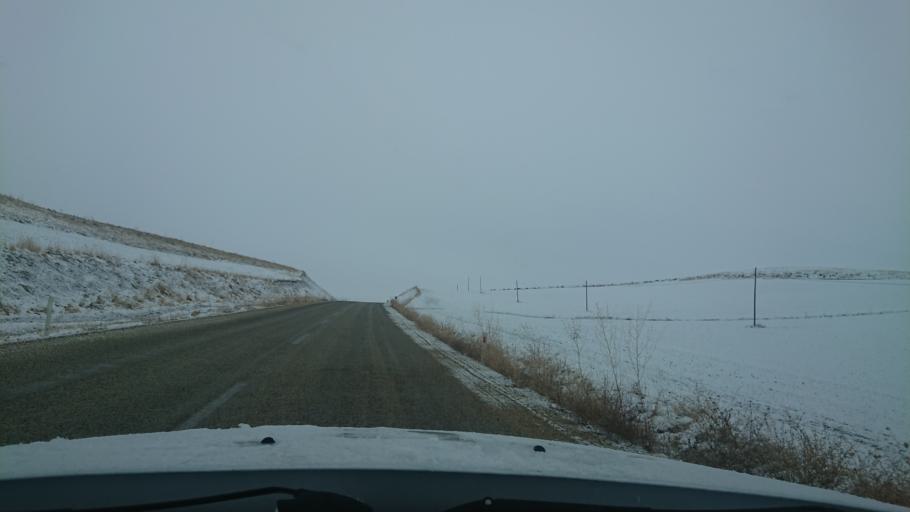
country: TR
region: Aksaray
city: Agacoren
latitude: 38.7899
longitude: 33.8710
